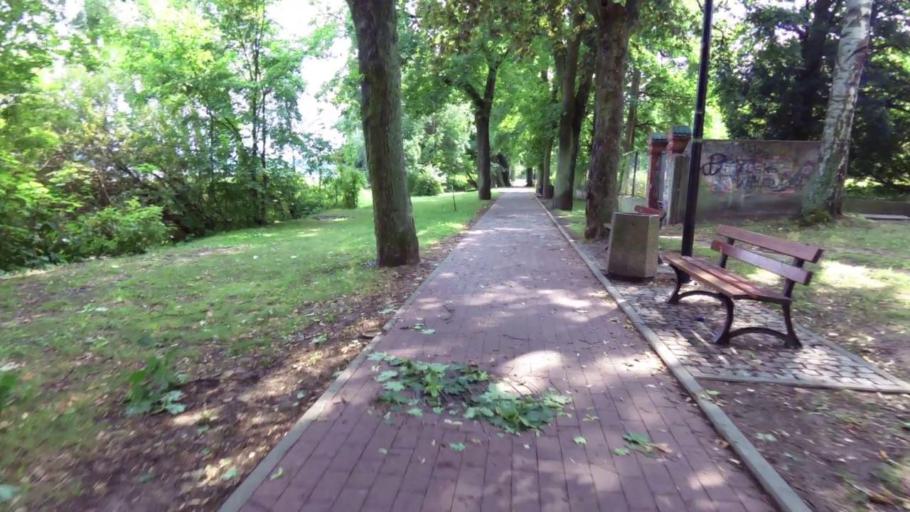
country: PL
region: West Pomeranian Voivodeship
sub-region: Powiat choszczenski
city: Choszczno
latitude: 53.1637
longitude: 15.4088
